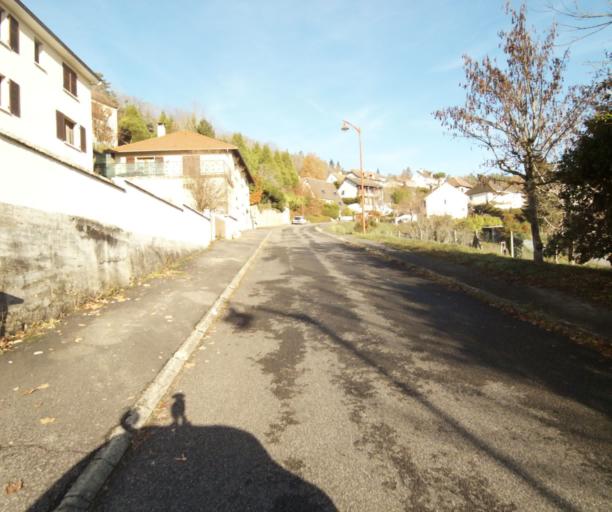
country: FR
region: Limousin
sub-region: Departement de la Correze
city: Laguenne
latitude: 45.2501
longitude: 1.7836
